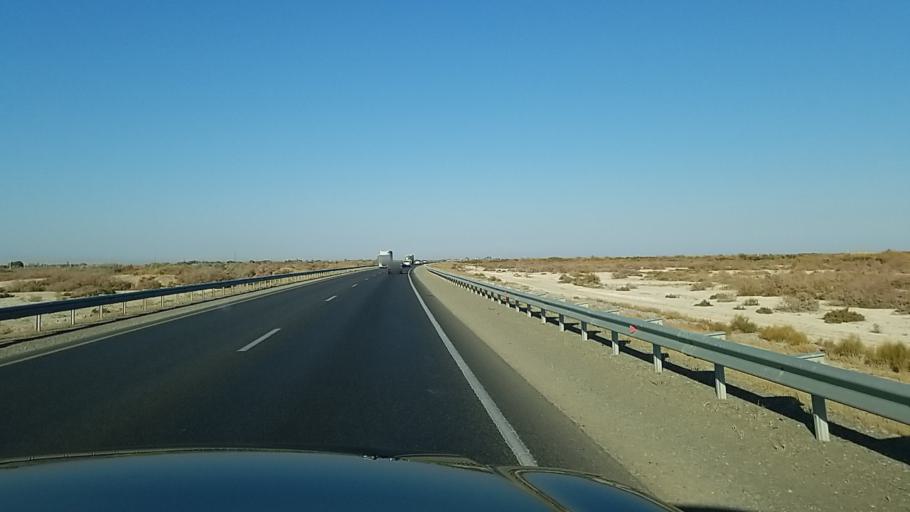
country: KZ
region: Qyzylorda
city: Terenozek
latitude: 44.8955
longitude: 65.0017
